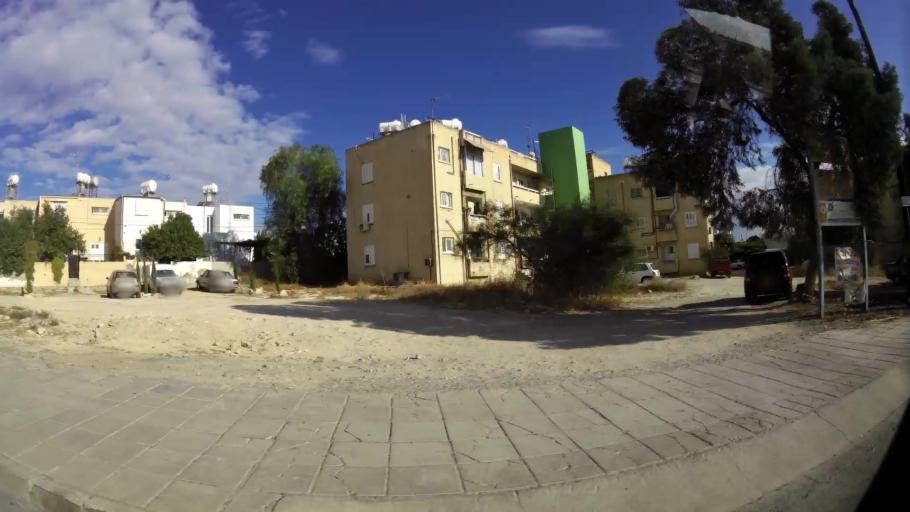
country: CY
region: Lefkosia
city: Nicosia
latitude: 35.1298
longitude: 33.3628
